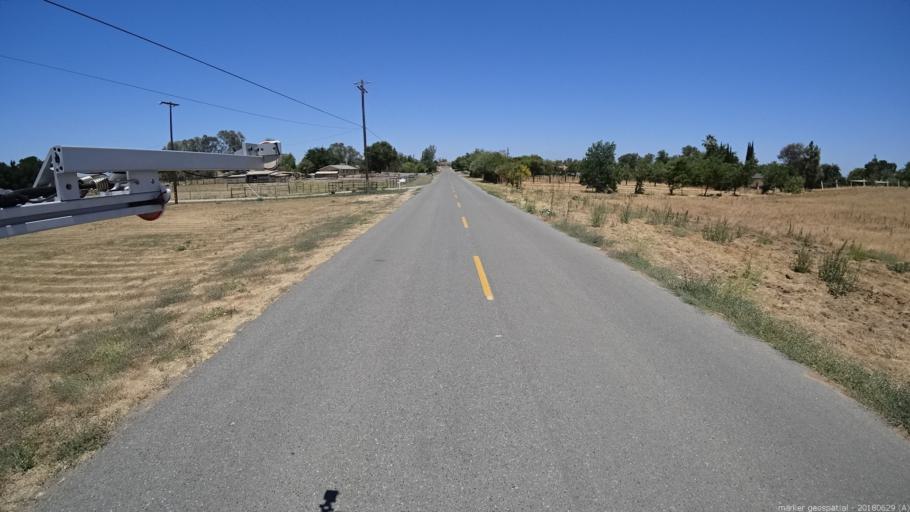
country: US
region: California
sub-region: Madera County
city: Parksdale
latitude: 36.9916
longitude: -119.9915
